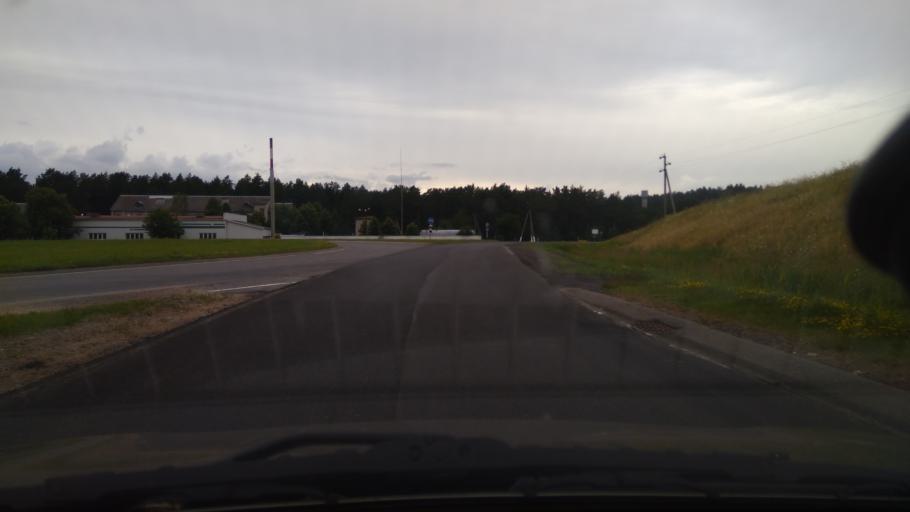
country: BY
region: Minsk
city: Rakaw
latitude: 53.9793
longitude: 27.0422
